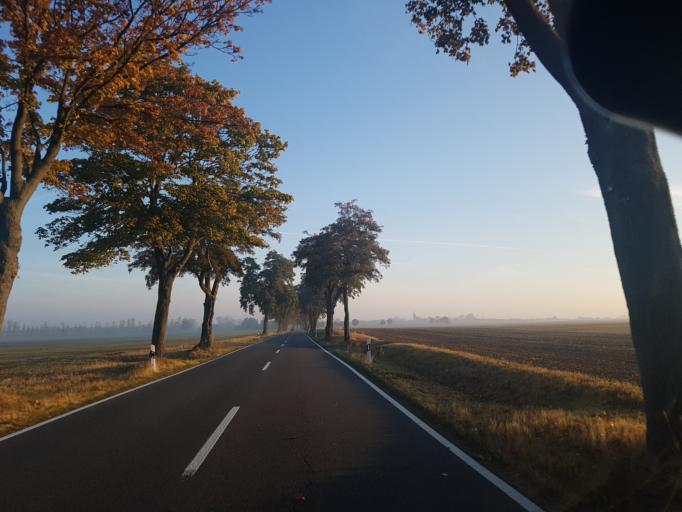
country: DE
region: Brandenburg
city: Juterbog
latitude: 51.9099
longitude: 13.0804
